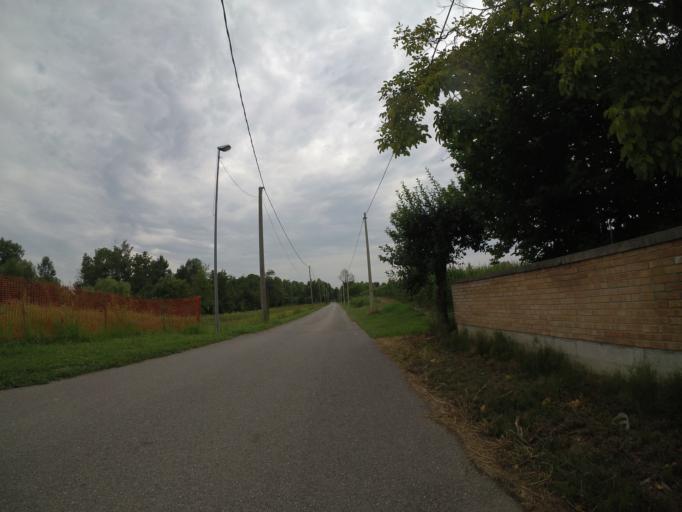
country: IT
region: Friuli Venezia Giulia
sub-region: Provincia di Udine
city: Rivignano
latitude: 45.8853
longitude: 13.0683
